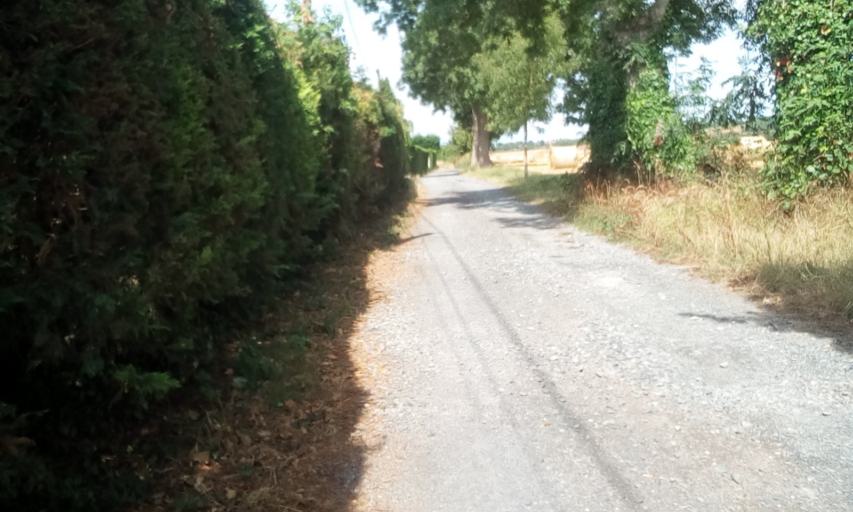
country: FR
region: Lower Normandy
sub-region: Departement du Calvados
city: Herouvillette
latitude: 49.2222
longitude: -0.2381
